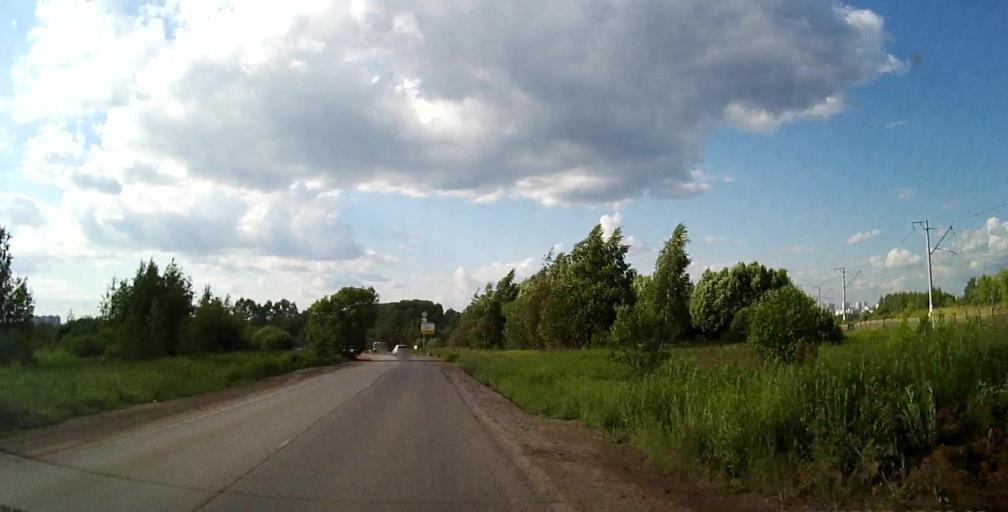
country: RU
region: Moskovskaya
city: Shcherbinka
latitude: 55.5219
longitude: 37.5340
